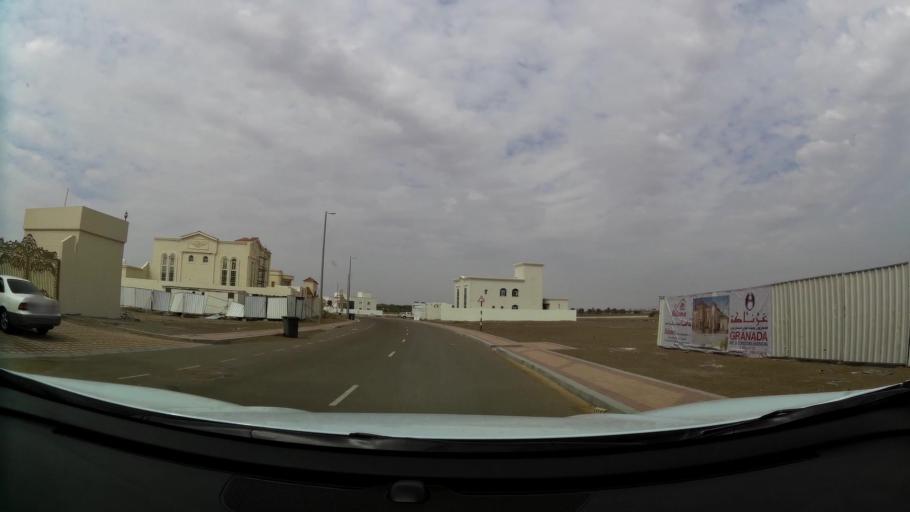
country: AE
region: Abu Dhabi
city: Al Ain
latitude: 24.1901
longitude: 55.8192
